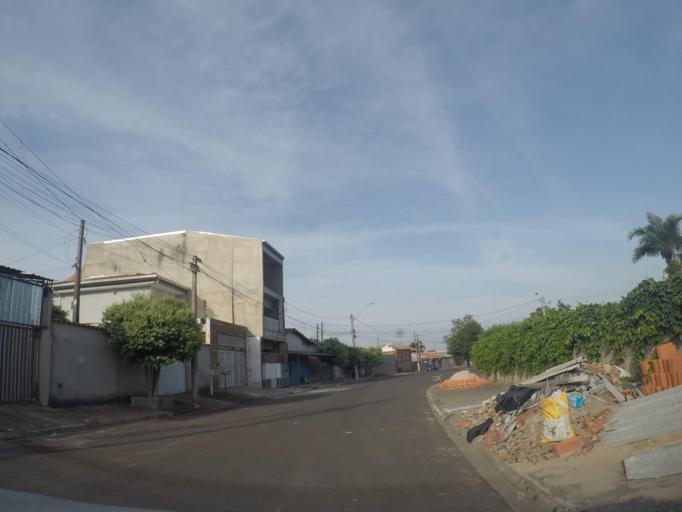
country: BR
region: Sao Paulo
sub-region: Hortolandia
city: Hortolandia
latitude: -22.8301
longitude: -47.1858
